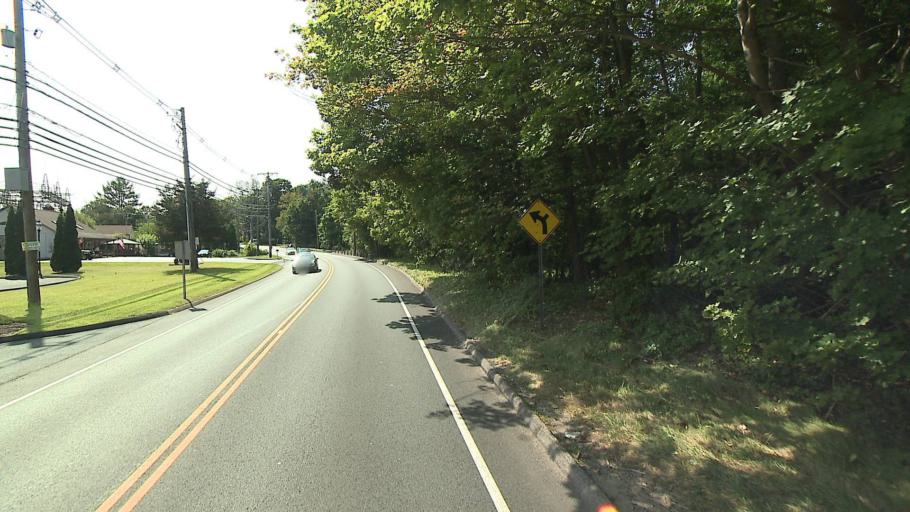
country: US
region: Connecticut
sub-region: Fairfield County
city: Newtown
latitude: 41.3921
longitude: -73.2910
